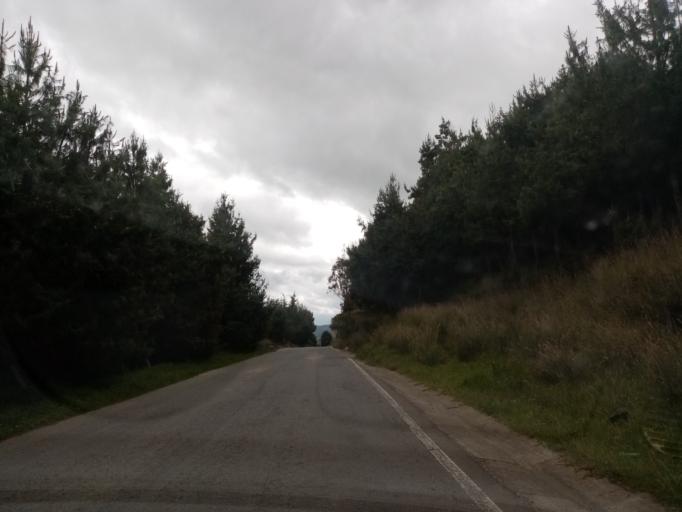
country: CO
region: Boyaca
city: Siachoque
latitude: 5.5737
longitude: -73.2723
